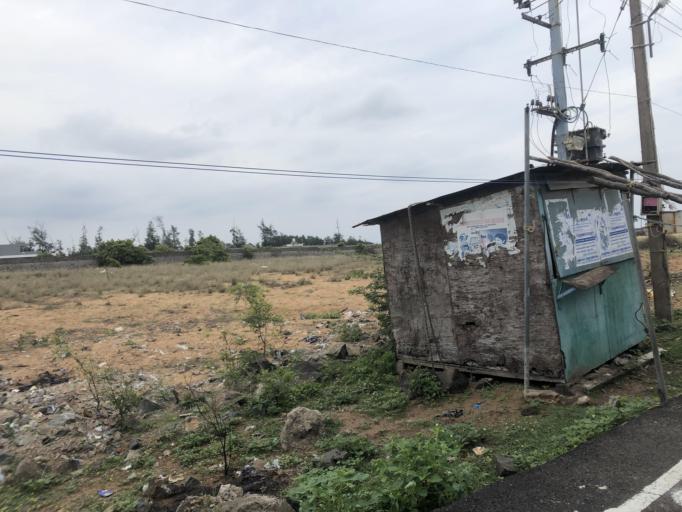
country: IN
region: Tamil Nadu
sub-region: Kancheepuram
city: Mamallapuram
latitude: 12.5992
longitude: 80.1883
